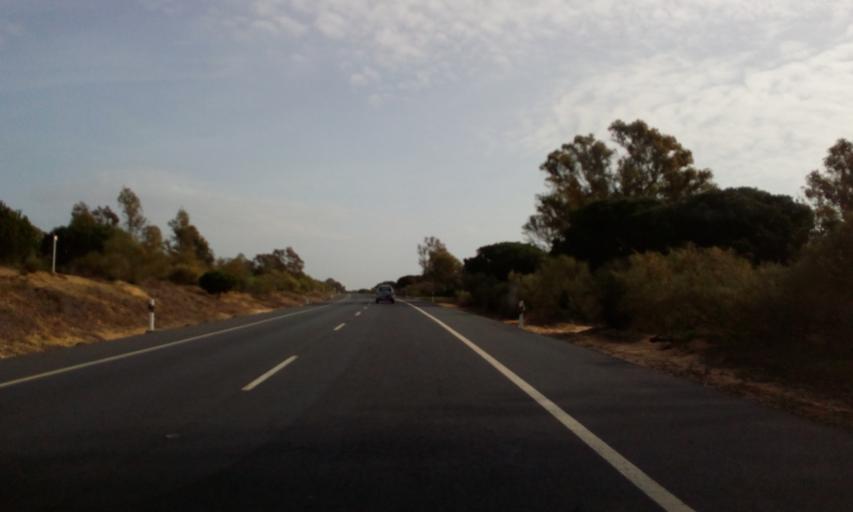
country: ES
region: Andalusia
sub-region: Provincia de Huelva
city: Palos de la Frontera
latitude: 37.1603
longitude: -6.8821
